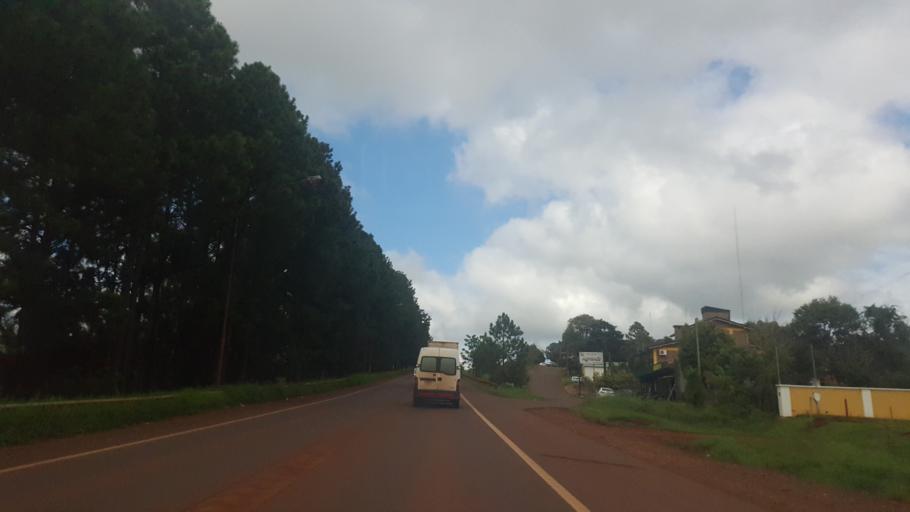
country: AR
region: Misiones
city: Aristobulo del Valle
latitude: -27.0847
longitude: -54.8256
